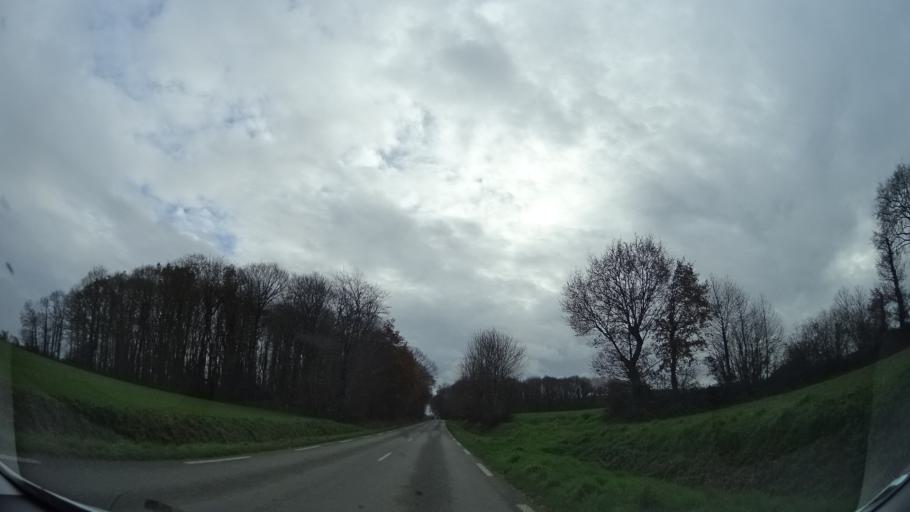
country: FR
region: Brittany
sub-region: Departement des Cotes-d'Armor
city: Evran
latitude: 48.3595
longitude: -1.9696
